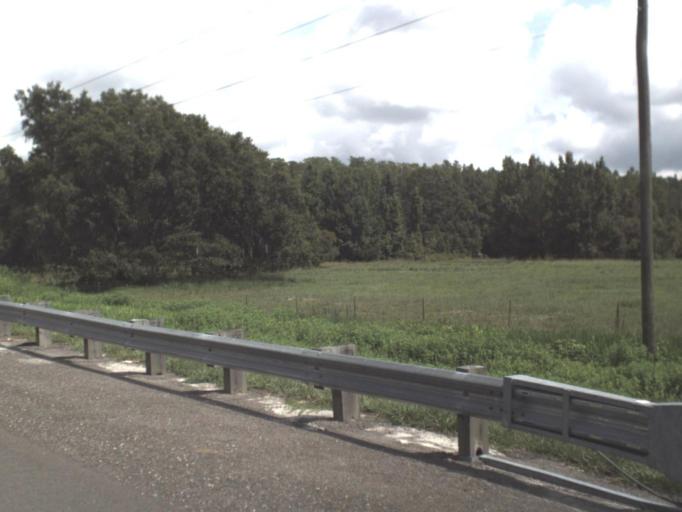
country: US
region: Florida
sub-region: Pasco County
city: Zephyrhills North
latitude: 28.2634
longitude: -82.0831
